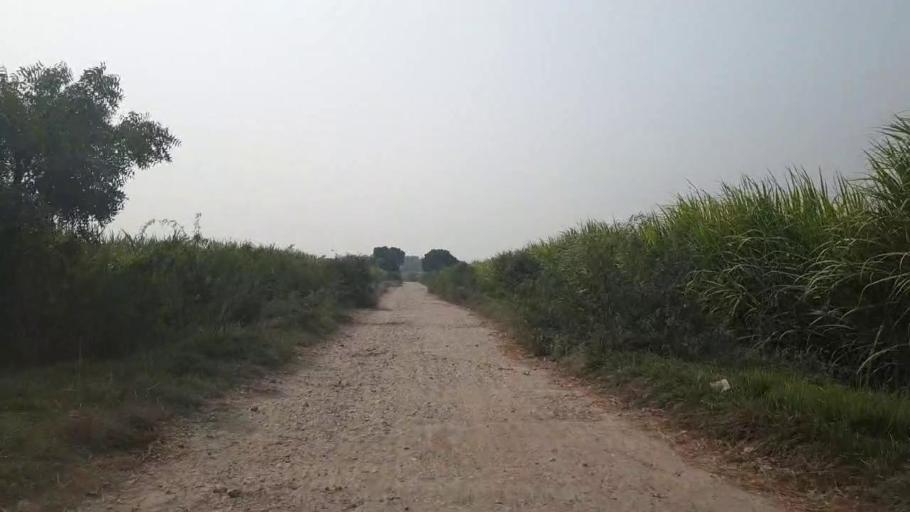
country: PK
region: Sindh
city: Tando Muhammad Khan
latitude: 25.2278
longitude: 68.5655
